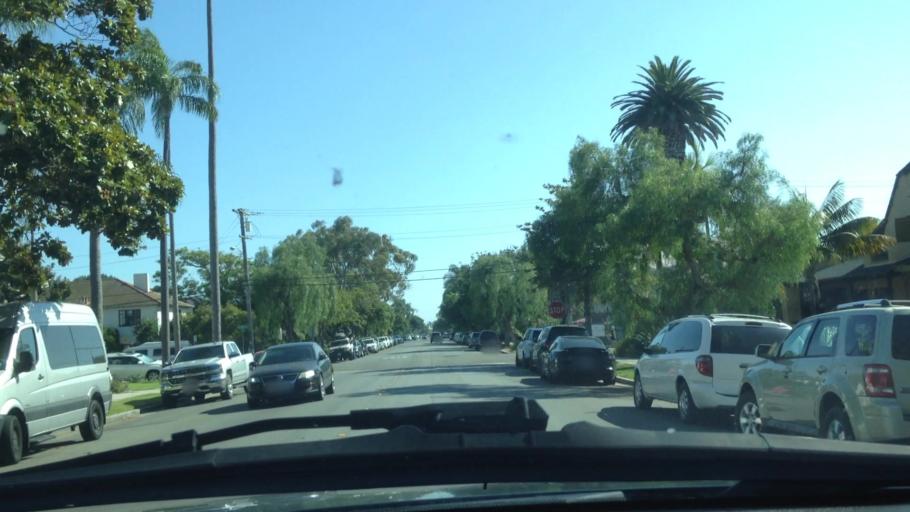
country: US
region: California
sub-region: San Diego County
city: Coronado
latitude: 32.6912
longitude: -117.1740
